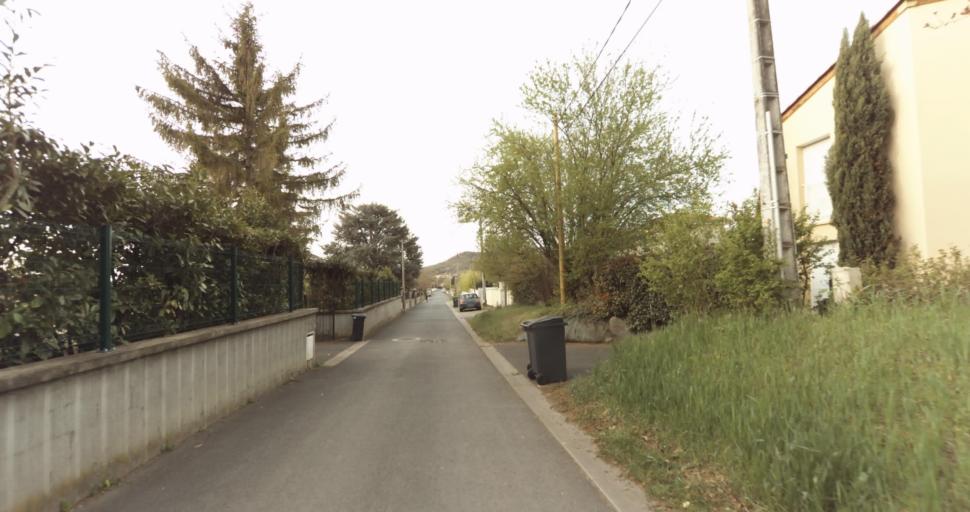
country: FR
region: Auvergne
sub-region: Departement du Puy-de-Dome
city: Cebazat
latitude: 45.8388
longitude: 3.0968
